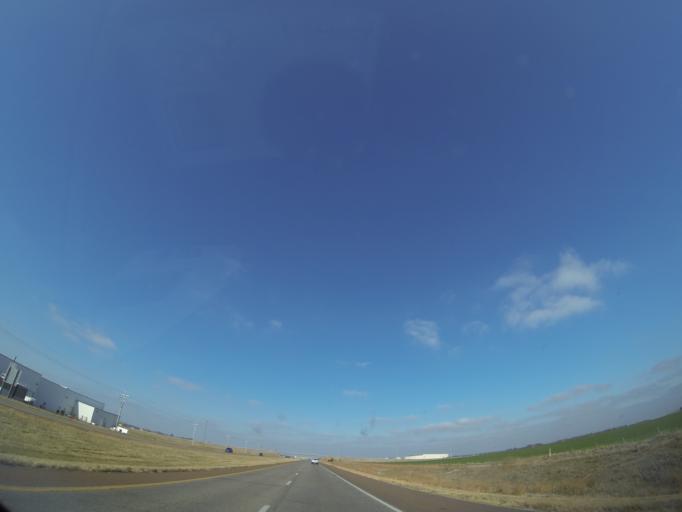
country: US
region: Kansas
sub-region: McPherson County
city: McPherson
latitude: 38.3876
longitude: -97.6205
